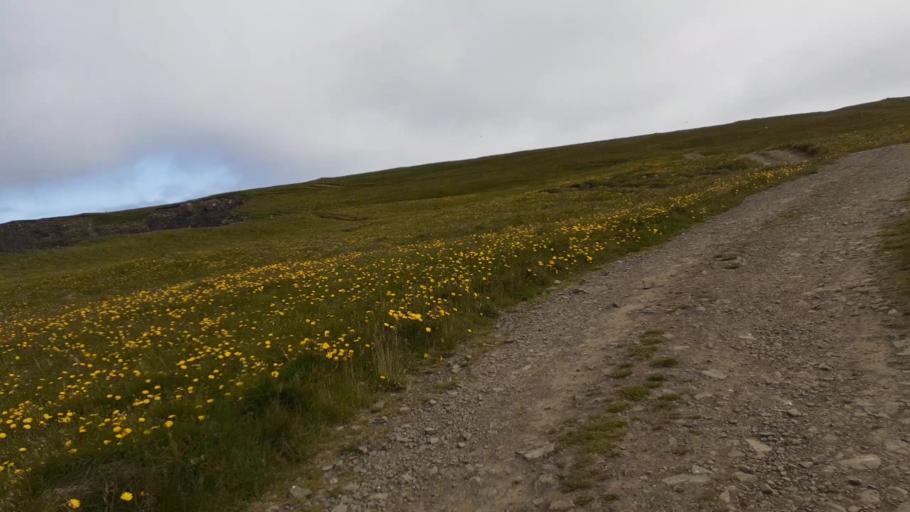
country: IS
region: Northeast
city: Dalvik
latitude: 66.5521
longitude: -18.0203
